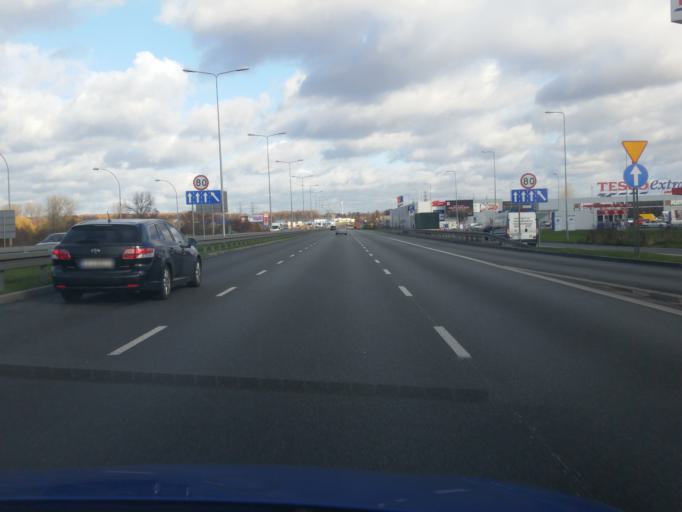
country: PL
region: Silesian Voivodeship
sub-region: Czestochowa
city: Czestochowa
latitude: 50.8216
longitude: 19.1405
